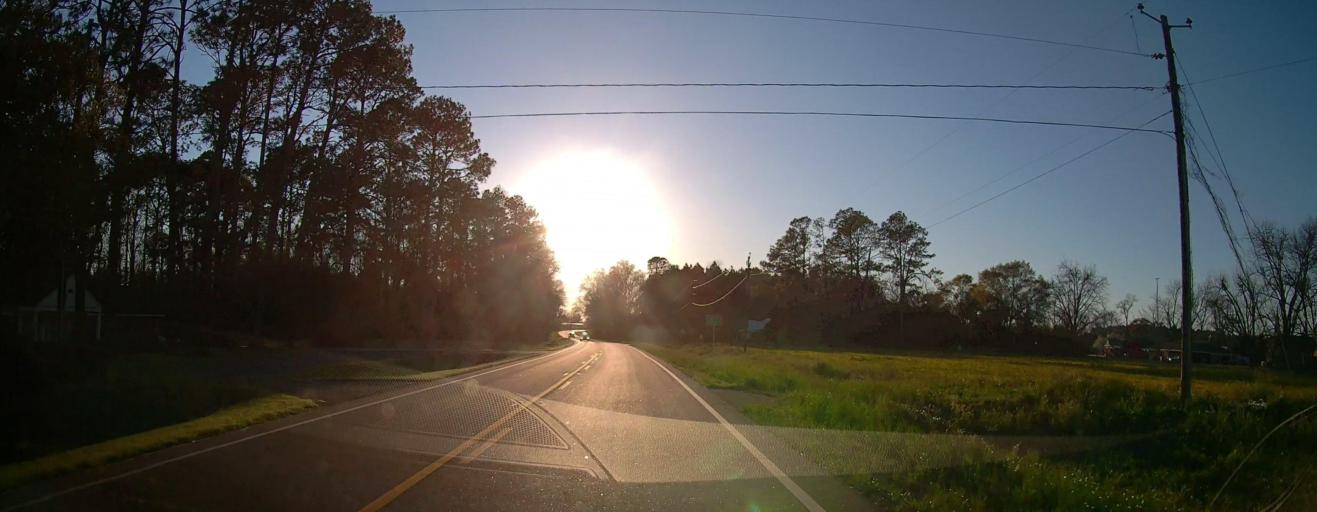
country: US
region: Georgia
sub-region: Wilcox County
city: Rochelle
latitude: 31.9456
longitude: -83.5326
